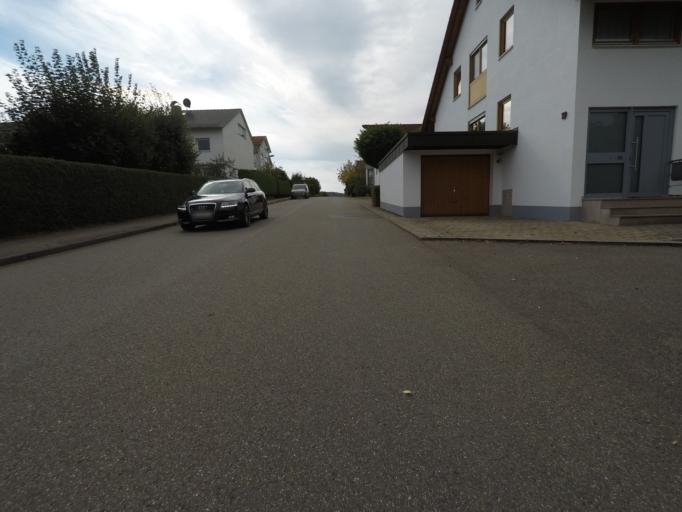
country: DE
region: Baden-Wuerttemberg
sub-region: Regierungsbezirk Stuttgart
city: Nufringen
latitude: 48.6257
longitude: 8.8872
